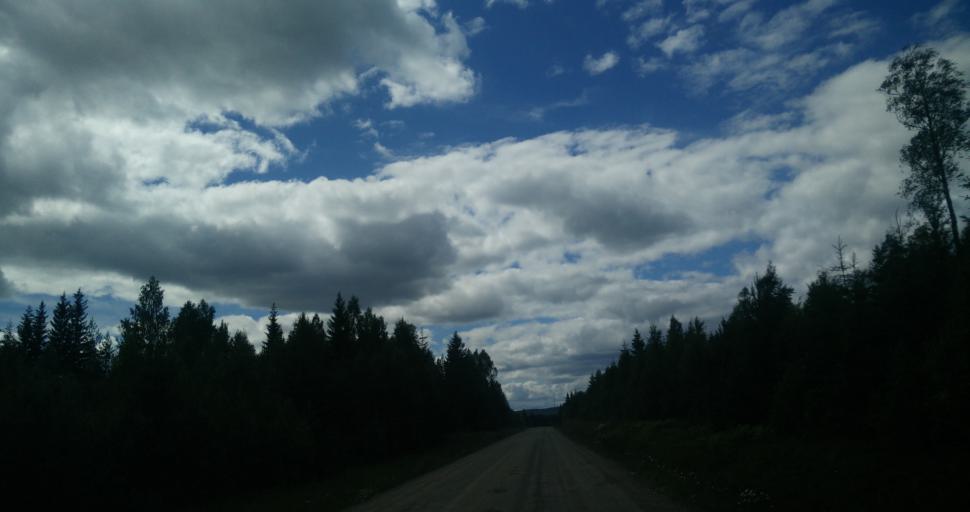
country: SE
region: Gaevleborg
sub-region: Nordanstigs Kommun
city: Bergsjoe
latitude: 62.1270
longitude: 17.1178
